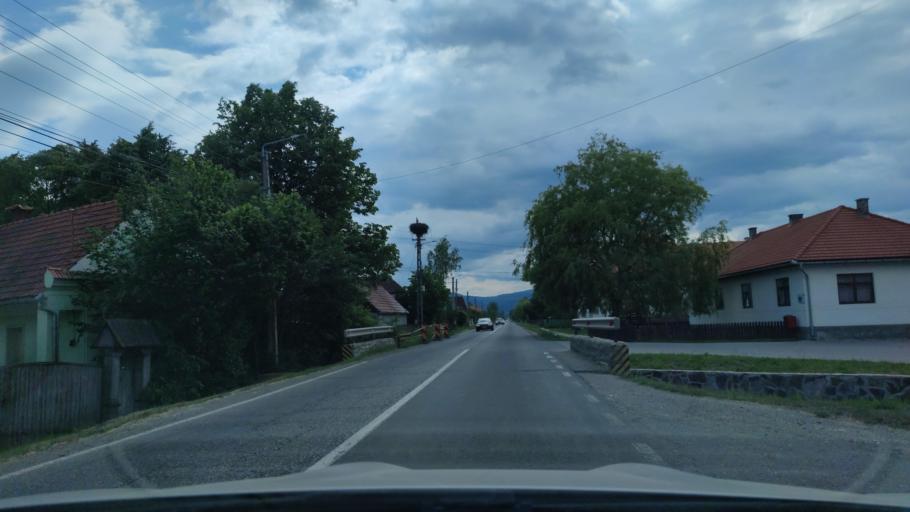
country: RO
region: Harghita
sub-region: Comuna Joseni
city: Joseni
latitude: 46.6944
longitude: 25.4471
